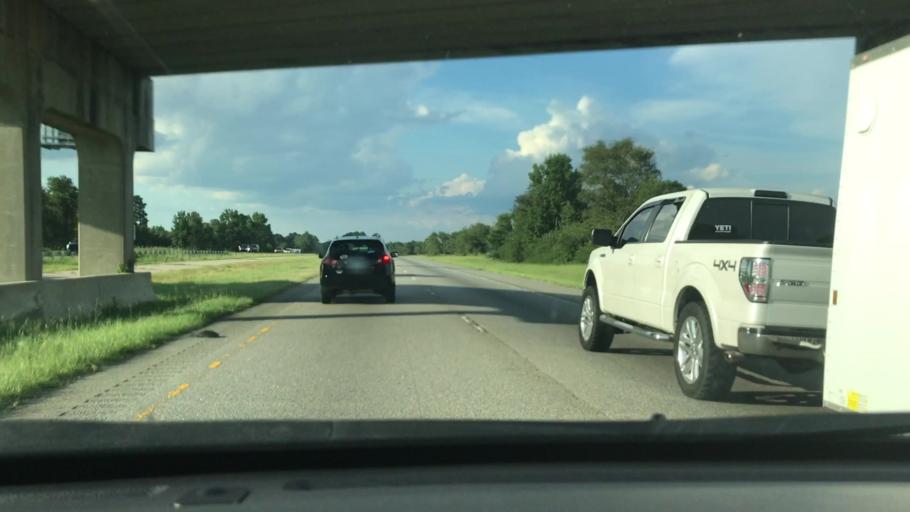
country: US
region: North Carolina
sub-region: Robeson County
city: Saint Pauls
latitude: 34.8474
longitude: -78.9698
